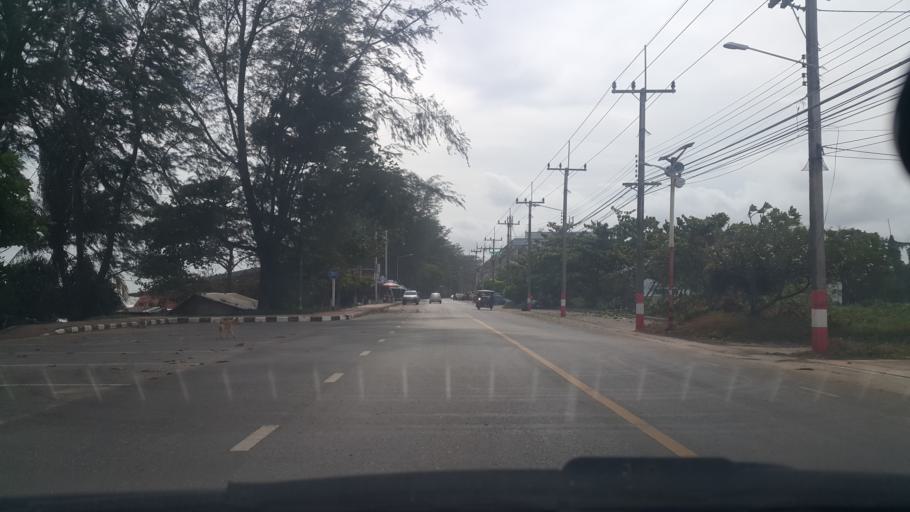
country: TH
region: Rayong
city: Rayong
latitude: 12.6220
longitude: 101.3646
